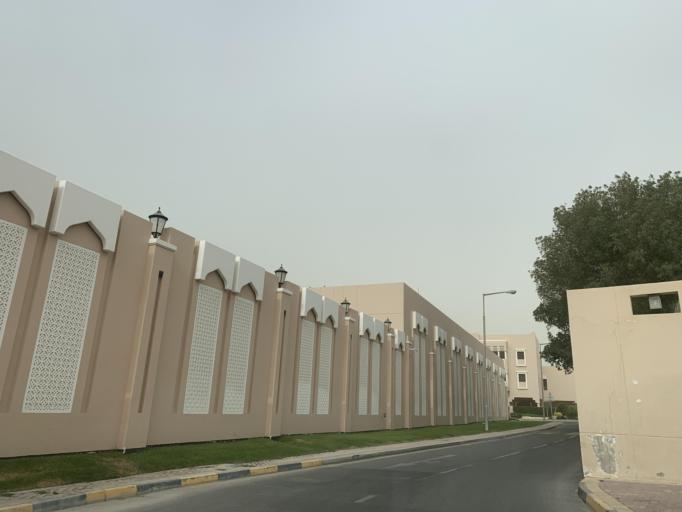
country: BH
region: Northern
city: Ar Rifa'
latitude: 26.1406
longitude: 50.5331
